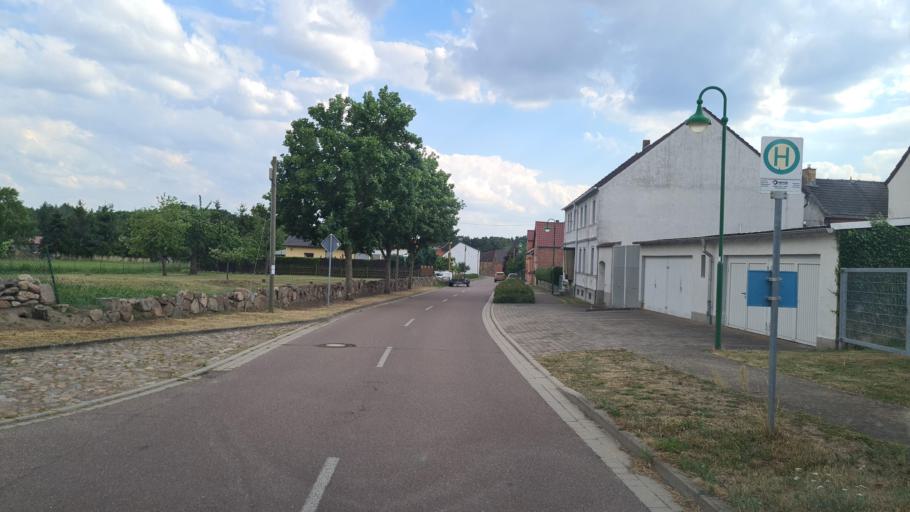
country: DE
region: Saxony-Anhalt
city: Kropstadt
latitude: 51.9747
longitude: 12.6818
